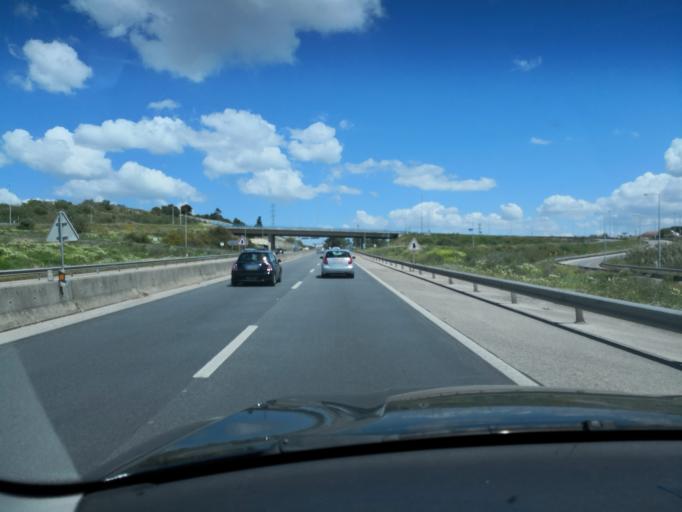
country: PT
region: Setubal
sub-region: Almada
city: Costa de Caparica
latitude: 38.6539
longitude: -9.2178
